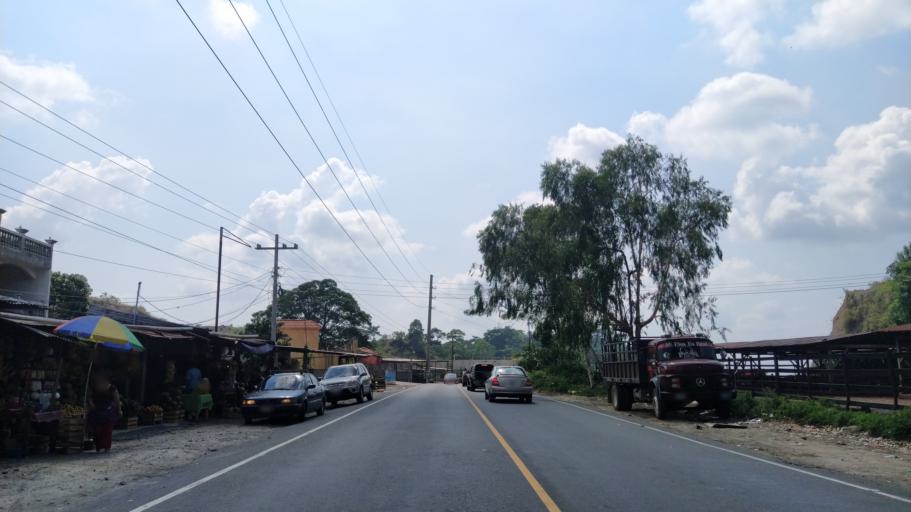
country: GT
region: Quetzaltenango
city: El Palmar
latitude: 14.6463
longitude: -91.5708
